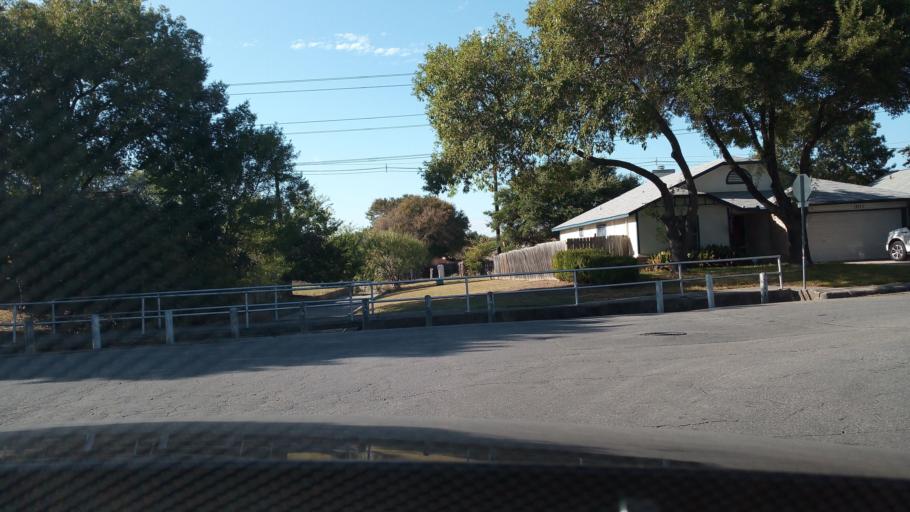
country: US
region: Texas
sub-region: Bexar County
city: Hollywood Park
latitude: 29.5619
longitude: -98.4385
